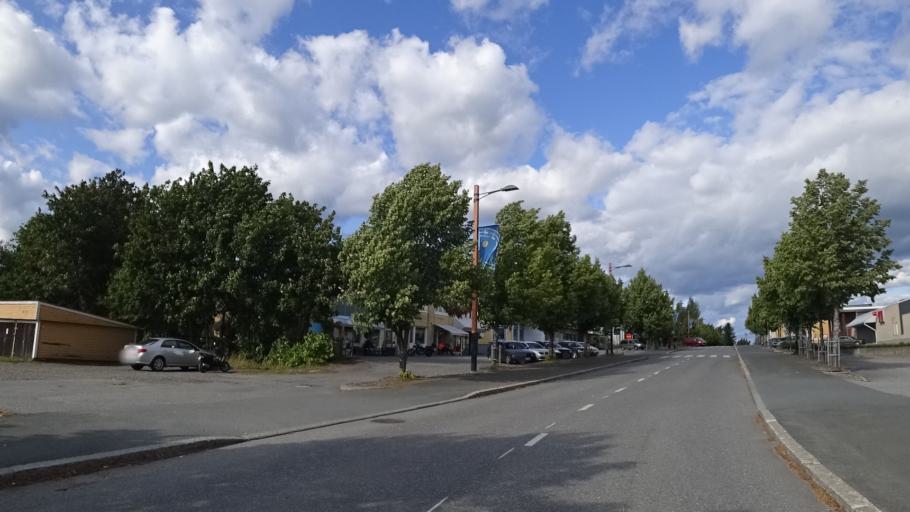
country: FI
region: North Karelia
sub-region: Keski-Karjala
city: Tohmajaervi
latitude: 62.2242
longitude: 30.3296
